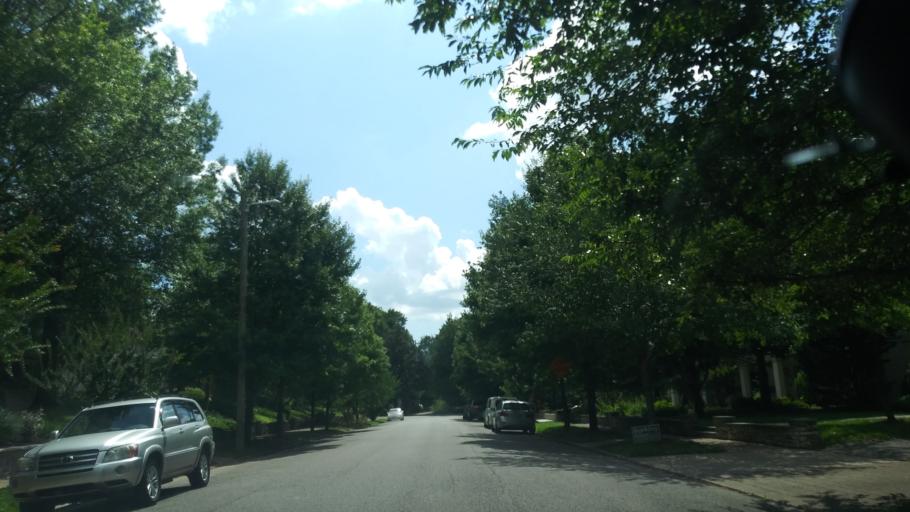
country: US
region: Tennessee
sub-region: Davidson County
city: Belle Meade
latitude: 36.1365
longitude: -86.8278
